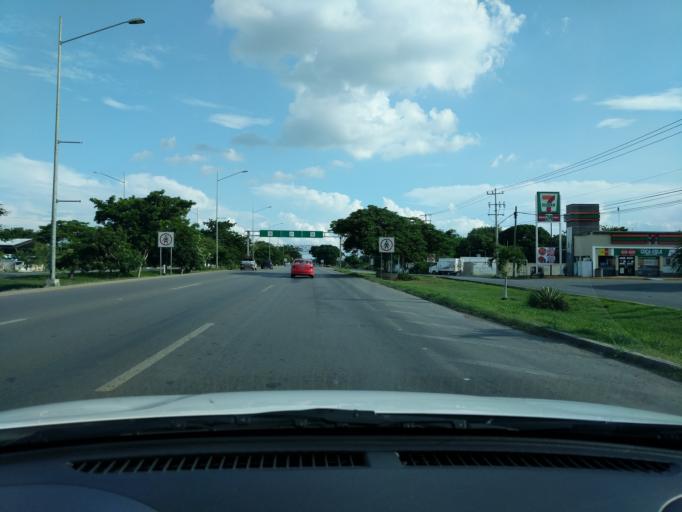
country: MX
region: Yucatan
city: Itzincab Palomeque
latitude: 20.9151
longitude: -89.6830
